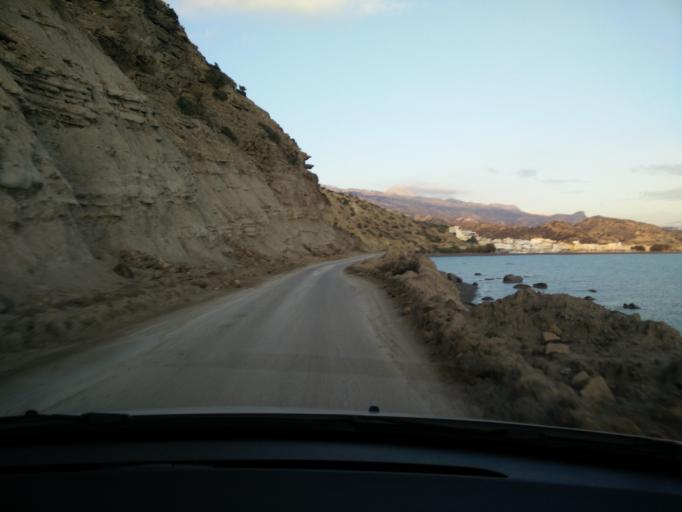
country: GR
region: Crete
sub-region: Nomos Lasithiou
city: Gra Liyia
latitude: 34.9998
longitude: 25.5767
